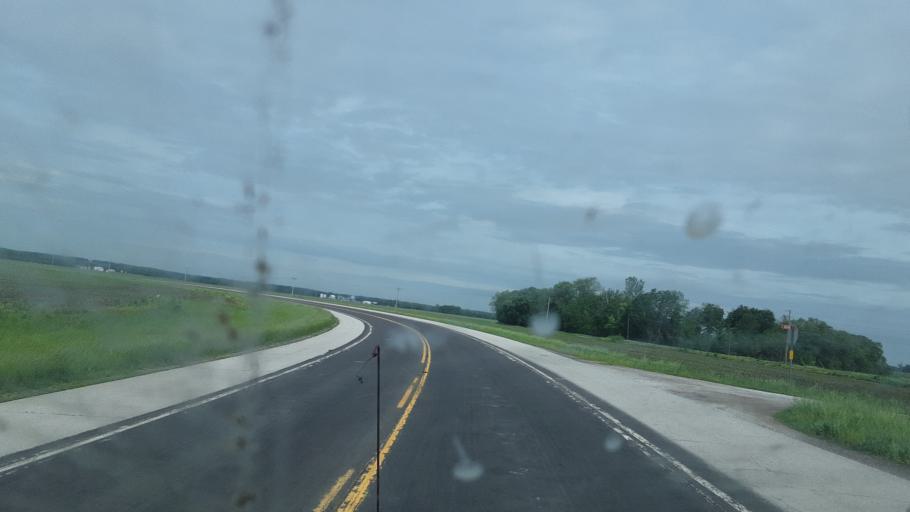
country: US
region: Illinois
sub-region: Hancock County
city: Warsaw
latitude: 40.3931
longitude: -91.5247
